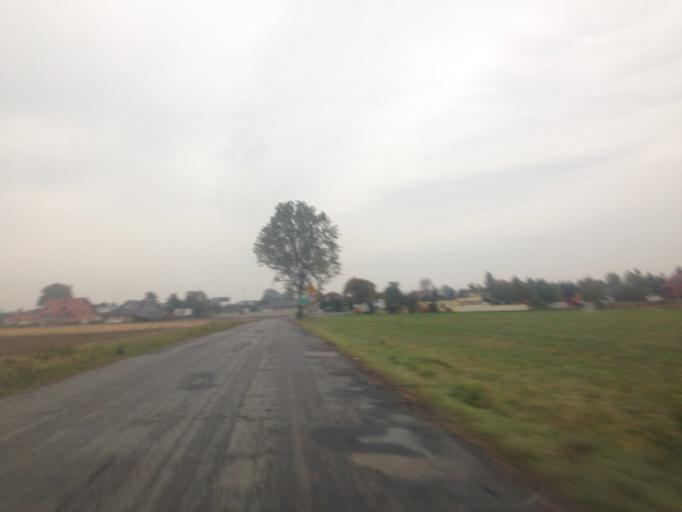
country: PL
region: Greater Poland Voivodeship
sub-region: Powiat poznanski
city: Kleszczewo
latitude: 52.3588
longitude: 17.1349
